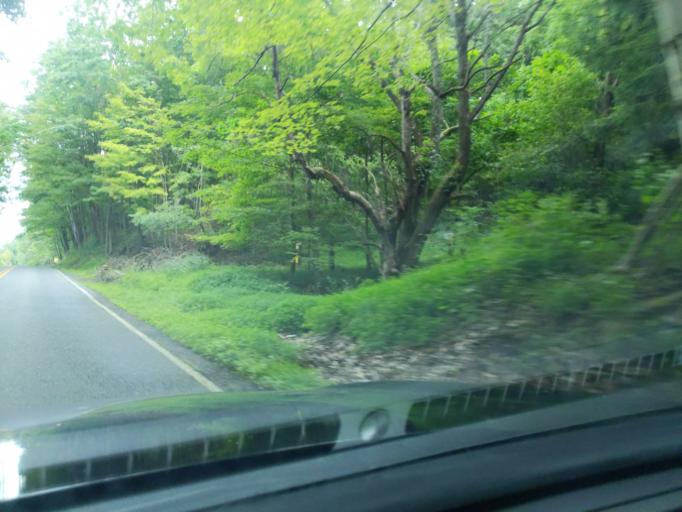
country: US
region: Pennsylvania
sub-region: Blair County
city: Claysburg
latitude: 40.3628
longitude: -78.5225
